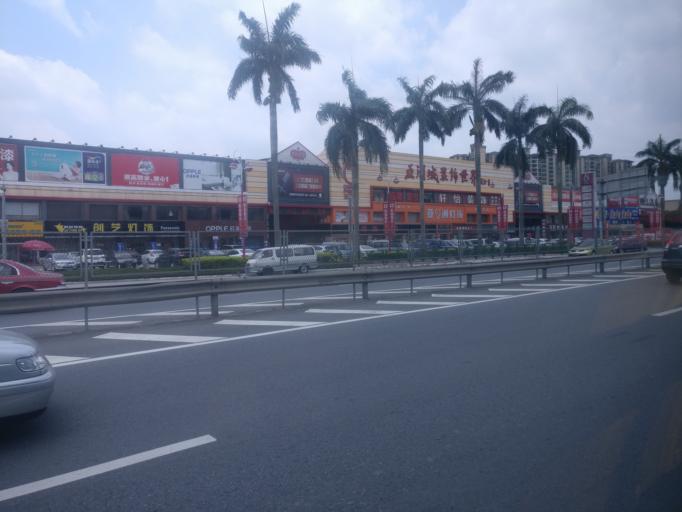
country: CN
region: Guangdong
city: Dashi
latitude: 23.0386
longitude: 113.3138
